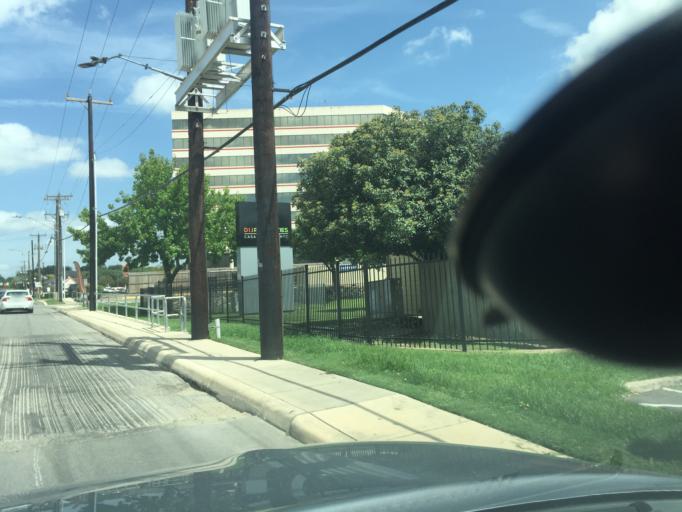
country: US
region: Texas
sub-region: Bexar County
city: Castle Hills
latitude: 29.5299
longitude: -98.4948
